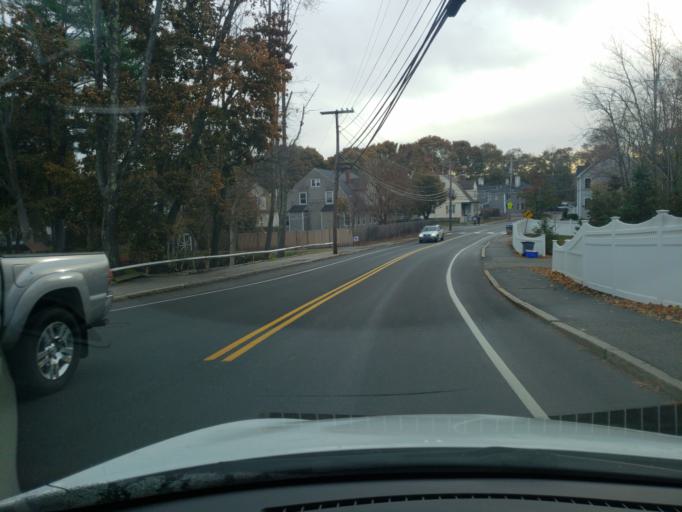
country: US
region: Massachusetts
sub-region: Essex County
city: Andover
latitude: 42.6593
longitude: -71.1496
